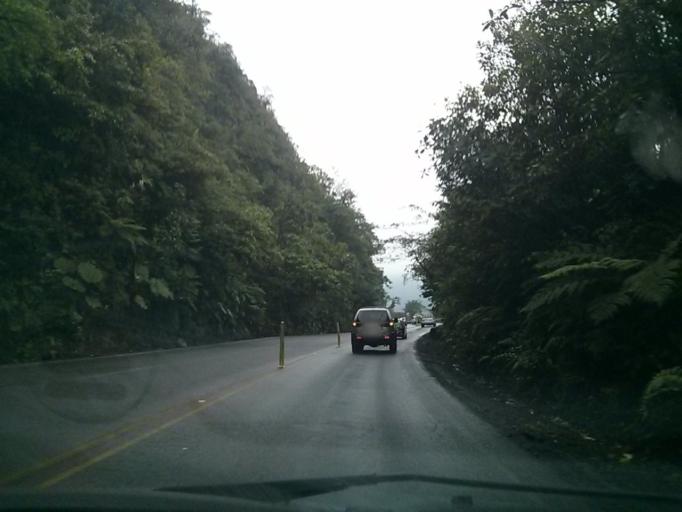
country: CR
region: San Jose
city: Dulce Nombre de Jesus
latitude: 10.0945
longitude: -83.9823
